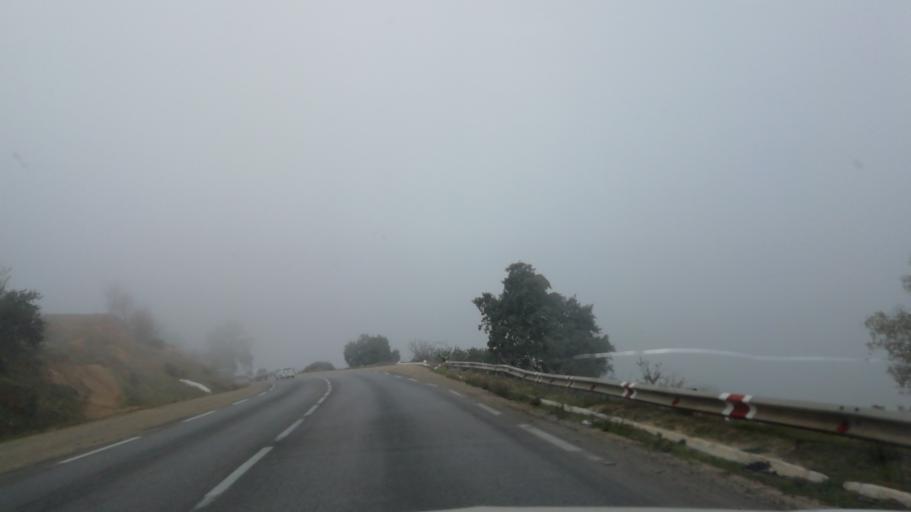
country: DZ
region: Mascara
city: Mascara
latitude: 35.5267
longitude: 0.3378
